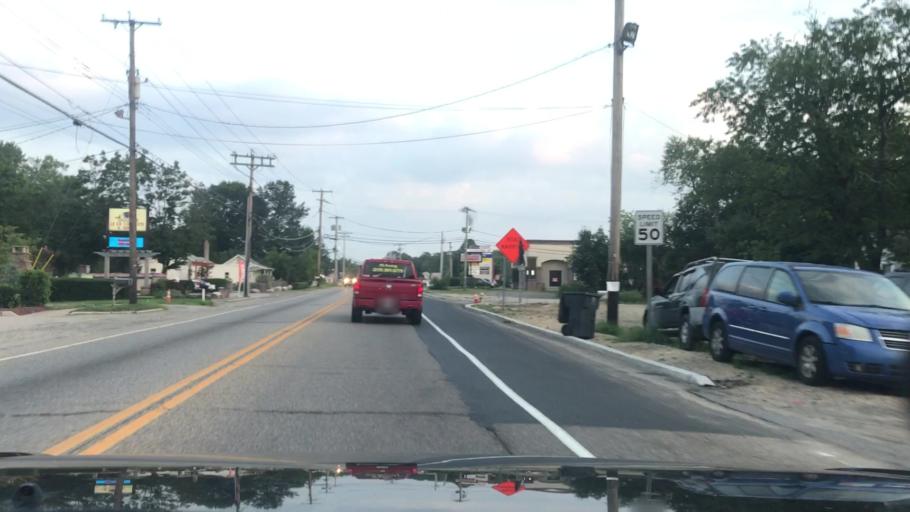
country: US
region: New Jersey
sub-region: Ocean County
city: Pine Lake Park
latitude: 40.0090
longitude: -74.2159
